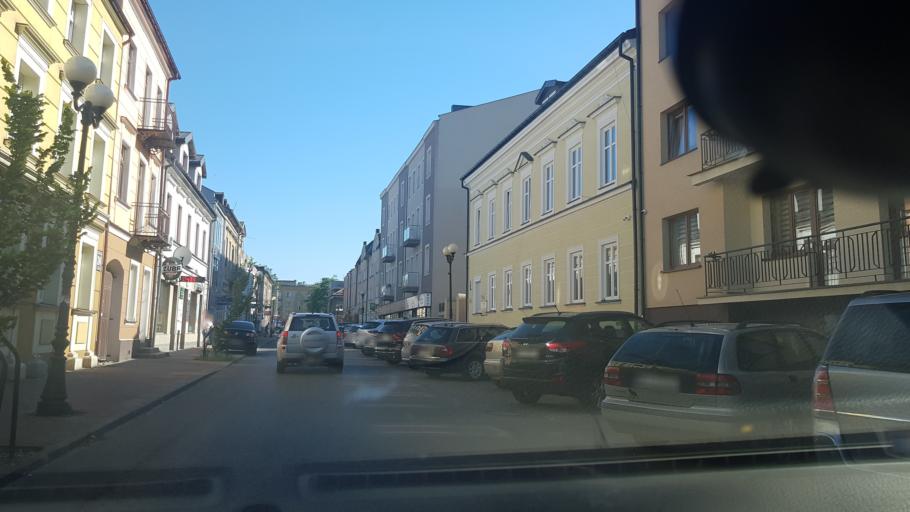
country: PL
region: Masovian Voivodeship
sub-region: Siedlce
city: Siedlce
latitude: 52.1693
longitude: 22.2752
